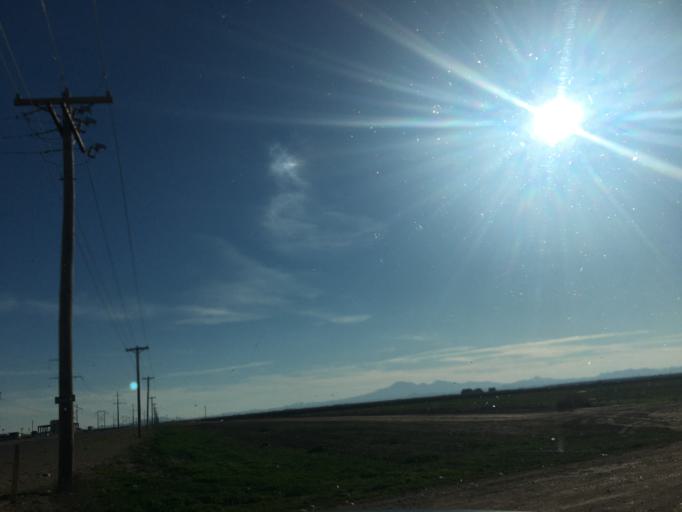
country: US
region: Arizona
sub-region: Pinal County
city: Maricopa
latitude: 33.0143
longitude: -111.9968
